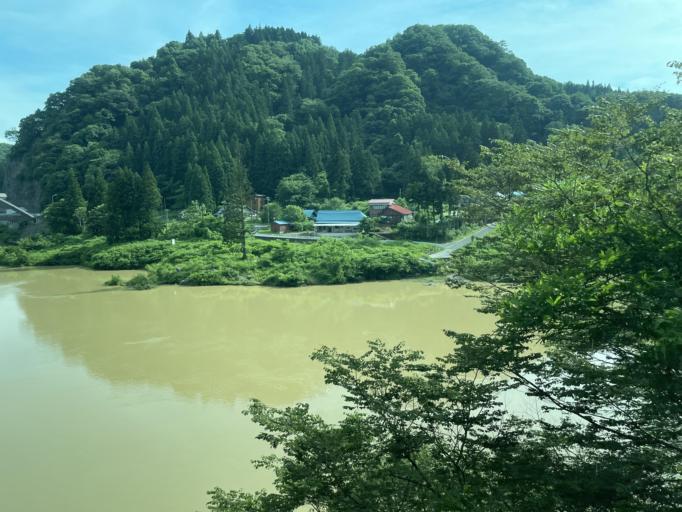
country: JP
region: Fukushima
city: Kitakata
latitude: 37.6712
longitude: 139.5910
